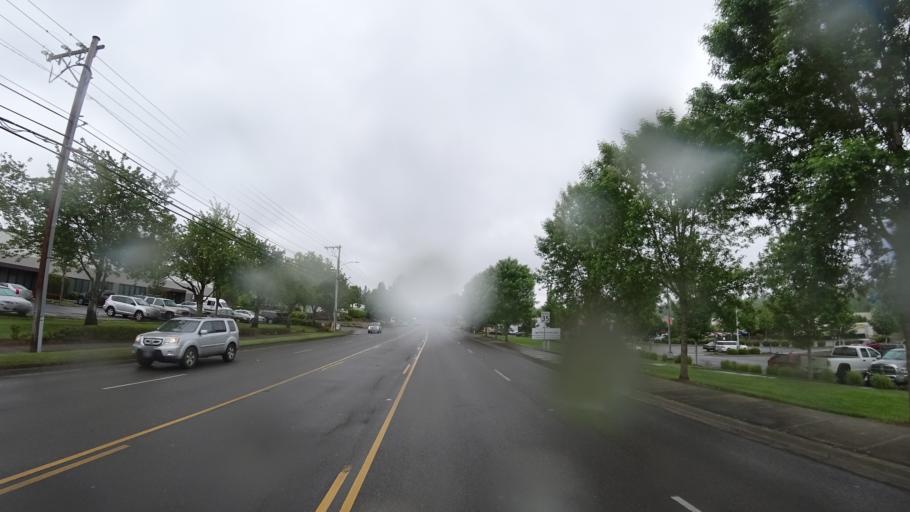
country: US
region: Oregon
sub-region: Washington County
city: Raleigh Hills
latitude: 45.4743
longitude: -122.7784
